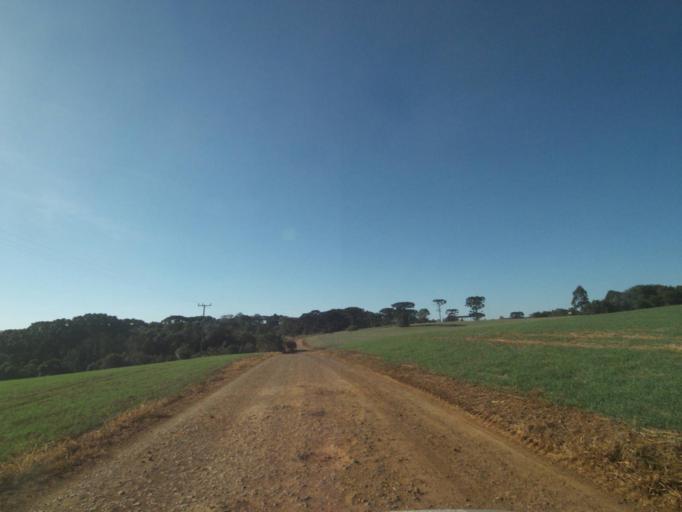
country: BR
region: Parana
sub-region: Tibagi
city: Tibagi
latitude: -24.5384
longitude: -50.4974
